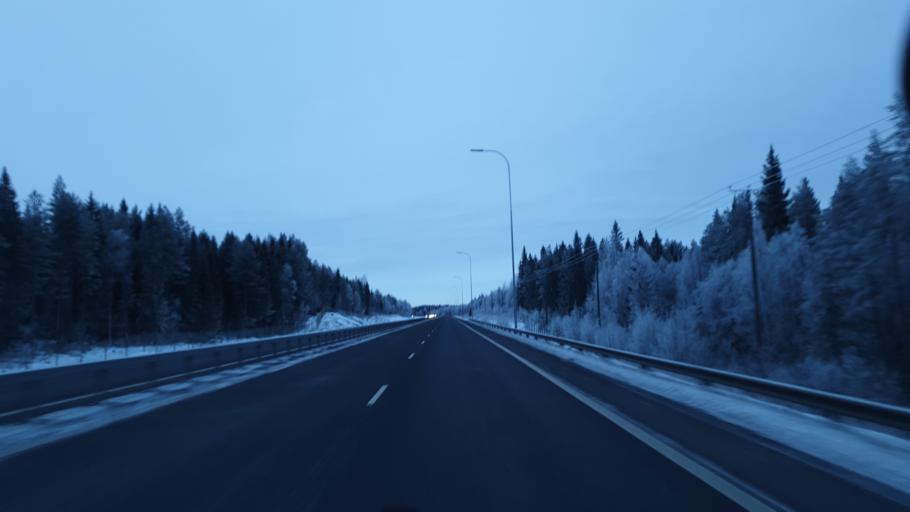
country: FI
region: Northern Ostrobothnia
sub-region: Oulu
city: Haukipudas
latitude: 65.2275
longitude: 25.3934
